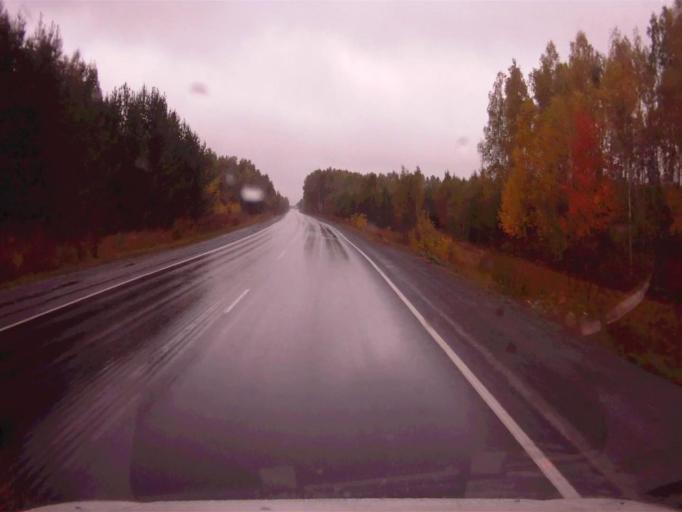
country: RU
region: Chelyabinsk
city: Tayginka
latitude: 55.5333
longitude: 60.6468
